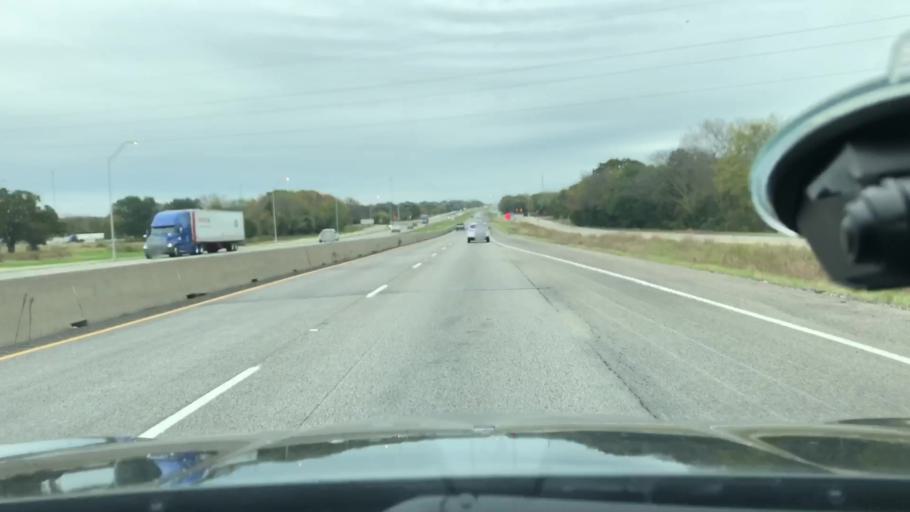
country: US
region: Texas
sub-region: Hunt County
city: Commerce
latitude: 33.1303
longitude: -95.8253
